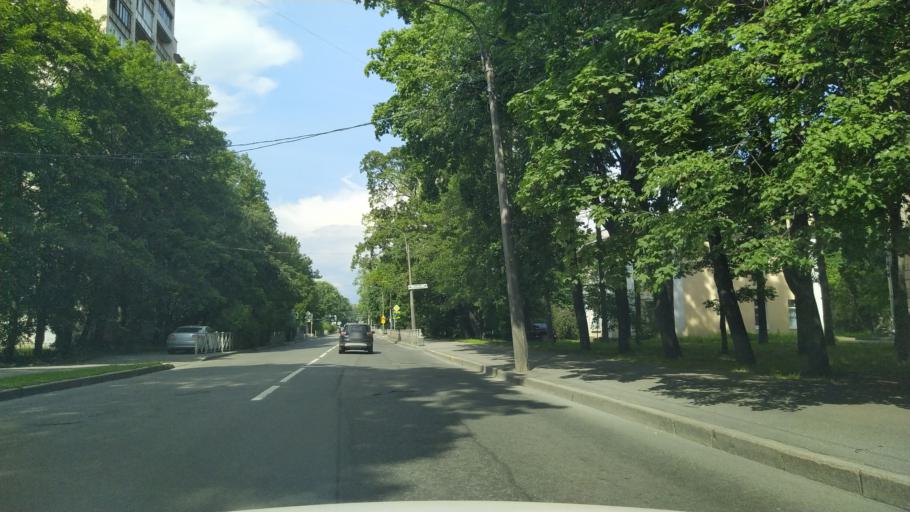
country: RU
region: Leningrad
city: Sampsonievskiy
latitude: 59.9976
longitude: 30.3463
